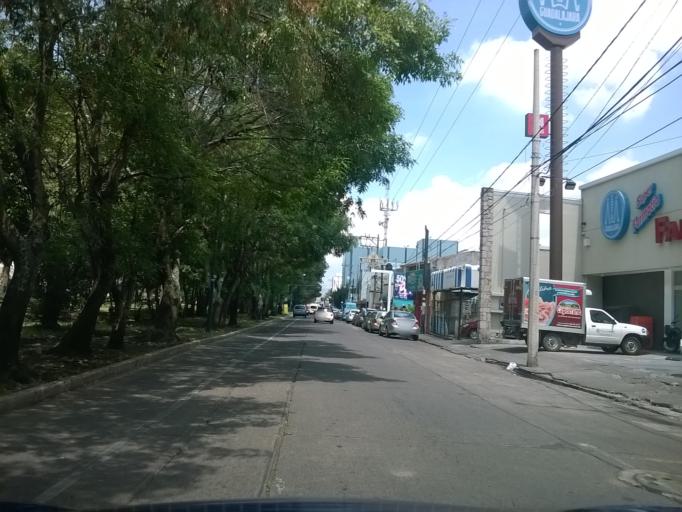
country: MX
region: Michoacan
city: Morelia
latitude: 19.6900
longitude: -101.1703
